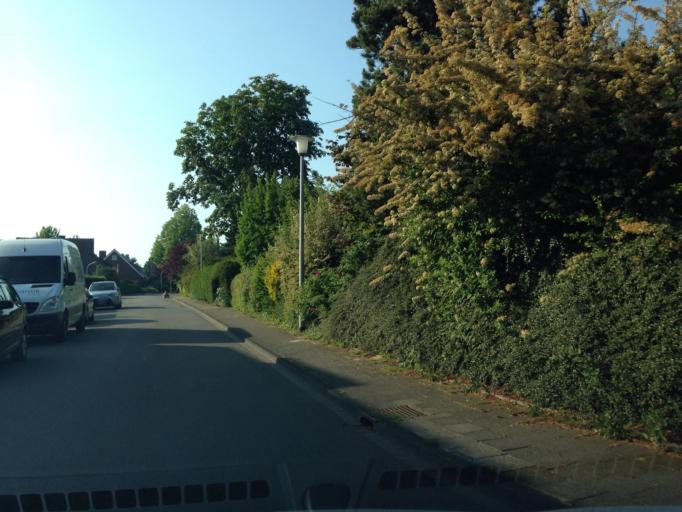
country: DE
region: North Rhine-Westphalia
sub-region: Regierungsbezirk Munster
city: Muenster
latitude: 51.9929
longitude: 7.5554
